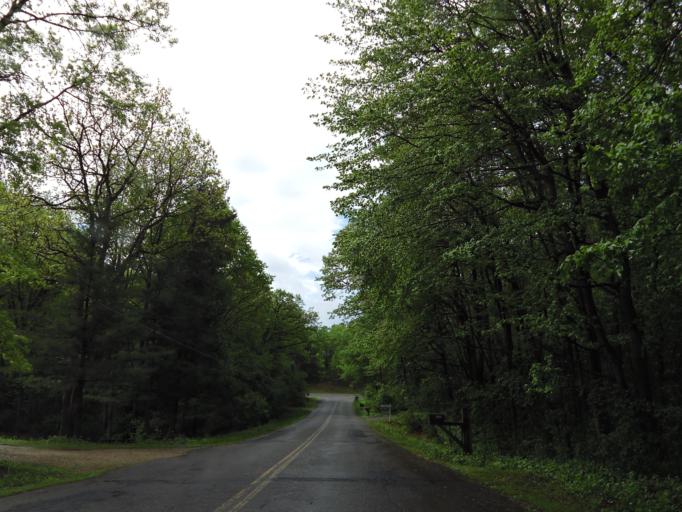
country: US
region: Minnesota
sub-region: Washington County
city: Lake Elmo
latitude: 44.9656
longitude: -92.8348
